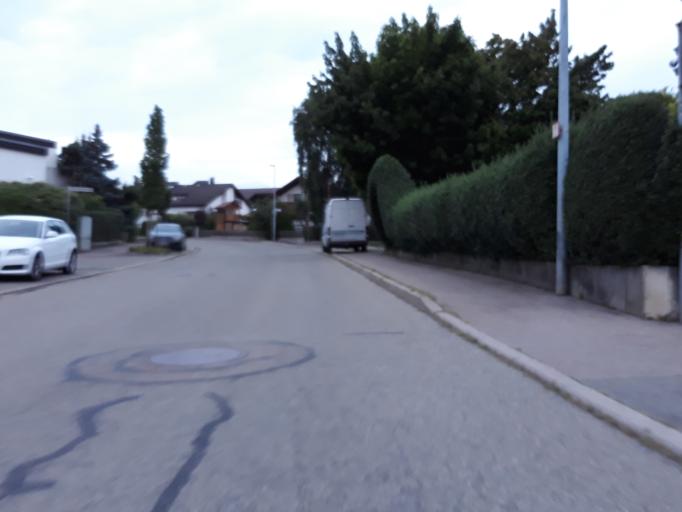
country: DE
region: Baden-Wuerttemberg
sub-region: Regierungsbezirk Stuttgart
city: Schonaich
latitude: 48.6672
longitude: 9.0631
